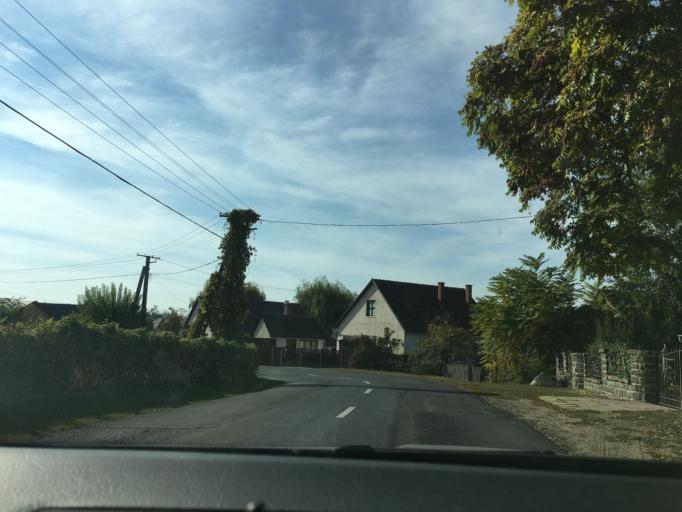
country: HU
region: Hajdu-Bihar
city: Nyirabrany
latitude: 47.5325
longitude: 21.9991
